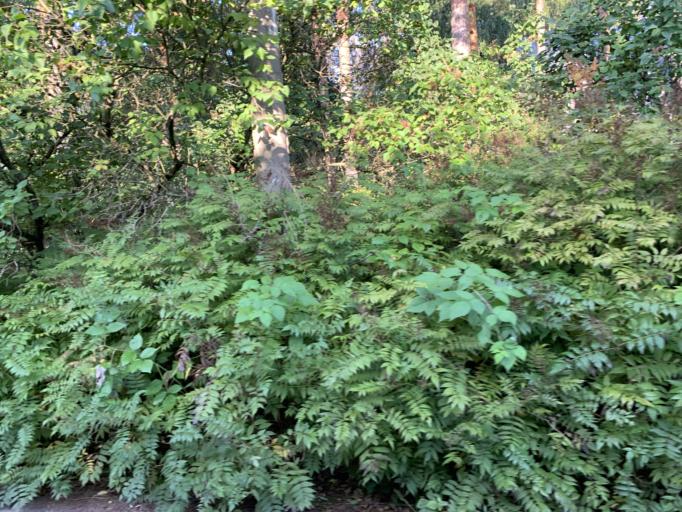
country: RU
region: Moskovskaya
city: Lesnyye Polyany
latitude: 55.9778
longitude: 37.8472
